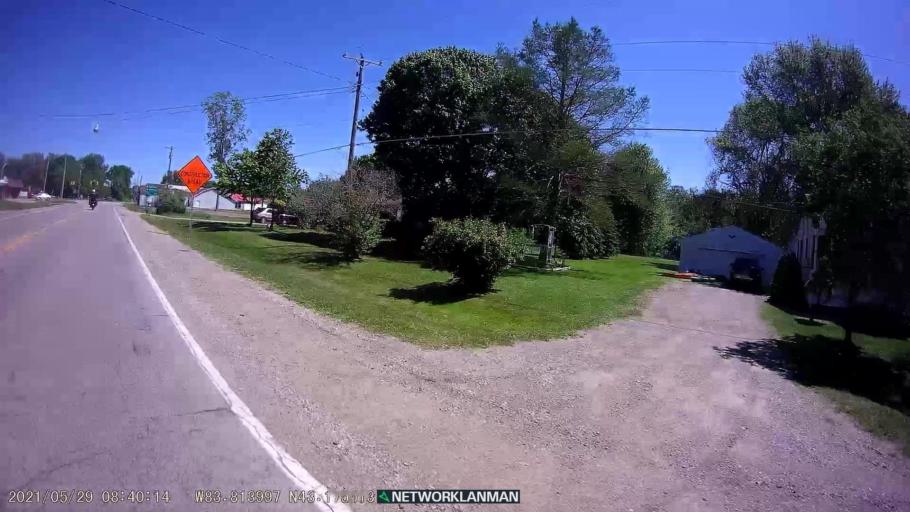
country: US
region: Michigan
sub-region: Saginaw County
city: Birch Run
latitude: 43.1758
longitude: -83.8140
